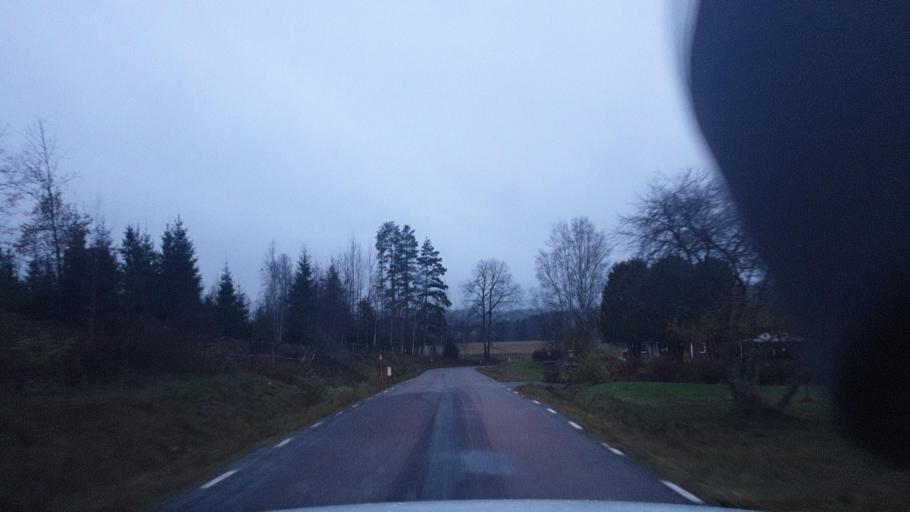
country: SE
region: Vaermland
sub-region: Eda Kommun
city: Amotfors
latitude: 59.6879
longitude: 12.1447
